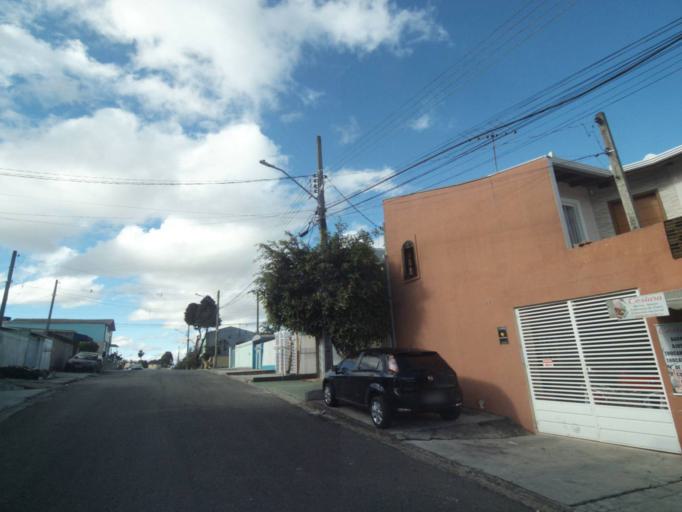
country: BR
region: Parana
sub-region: Sao Jose Dos Pinhais
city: Sao Jose dos Pinhais
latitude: -25.5318
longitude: -49.2839
